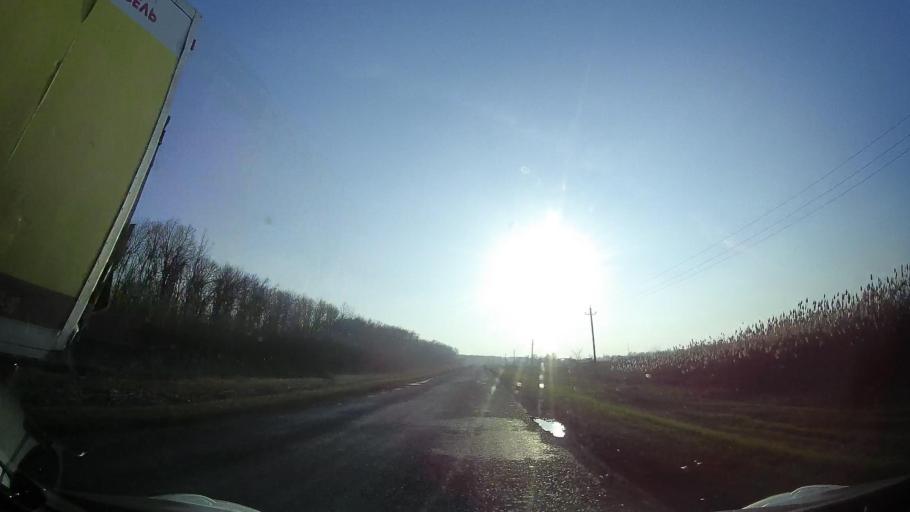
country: RU
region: Rostov
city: Ol'ginskaya
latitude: 47.1423
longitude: 39.9016
